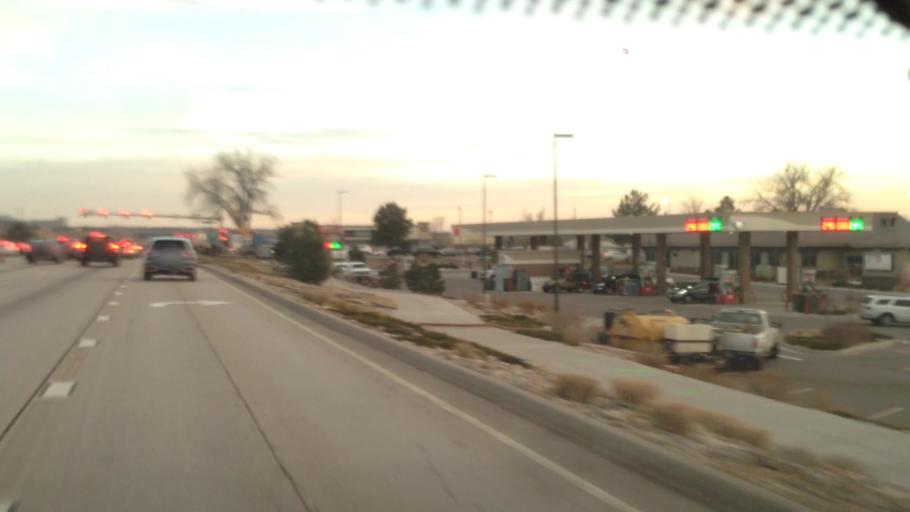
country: US
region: Colorado
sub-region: Douglas County
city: Stonegate
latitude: 39.5597
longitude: -104.7810
